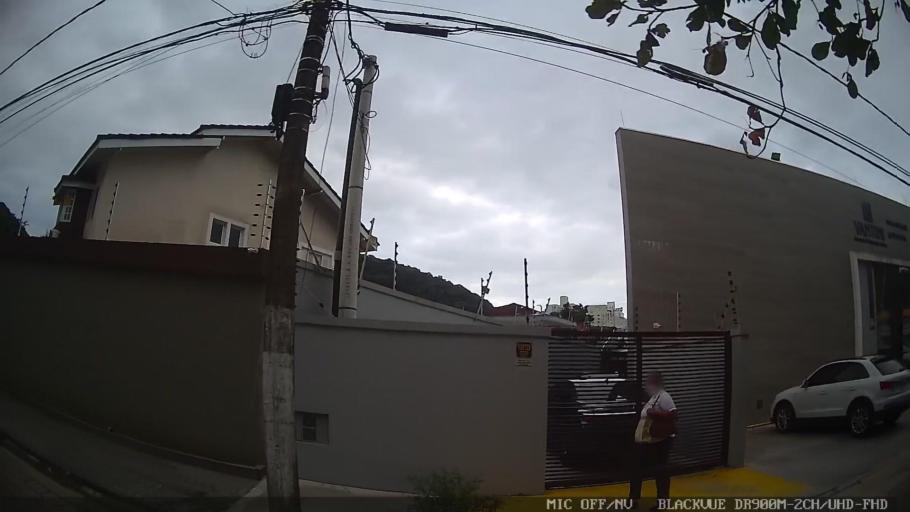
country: BR
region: Sao Paulo
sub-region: Guaruja
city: Guaruja
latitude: -23.9903
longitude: -46.2564
